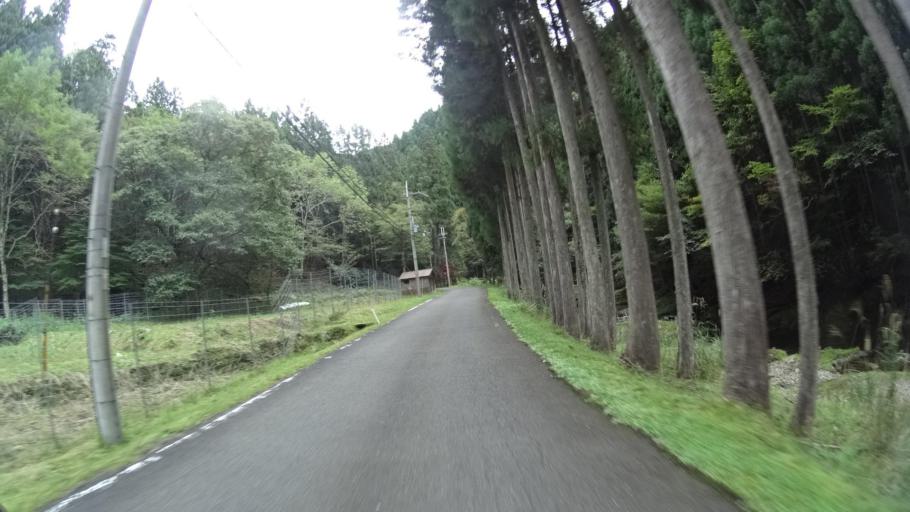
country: JP
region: Shiga Prefecture
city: Kitahama
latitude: 35.2330
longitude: 135.7905
